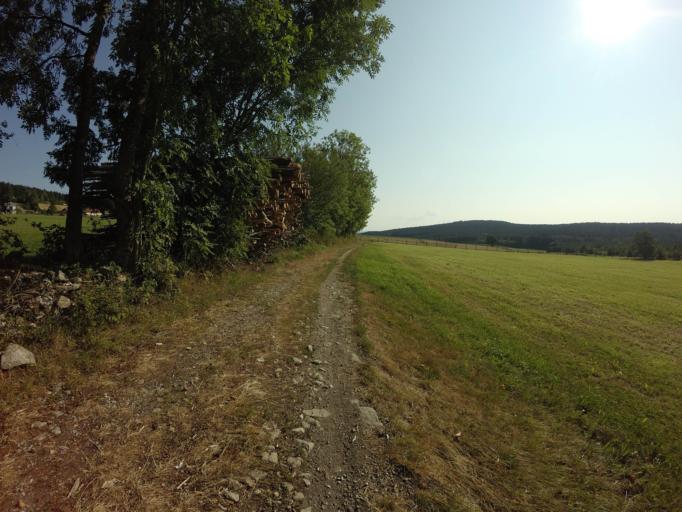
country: AT
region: Upper Austria
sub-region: Politischer Bezirk Urfahr-Umgebung
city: Bad Leonfelden
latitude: 48.5434
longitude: 14.3167
